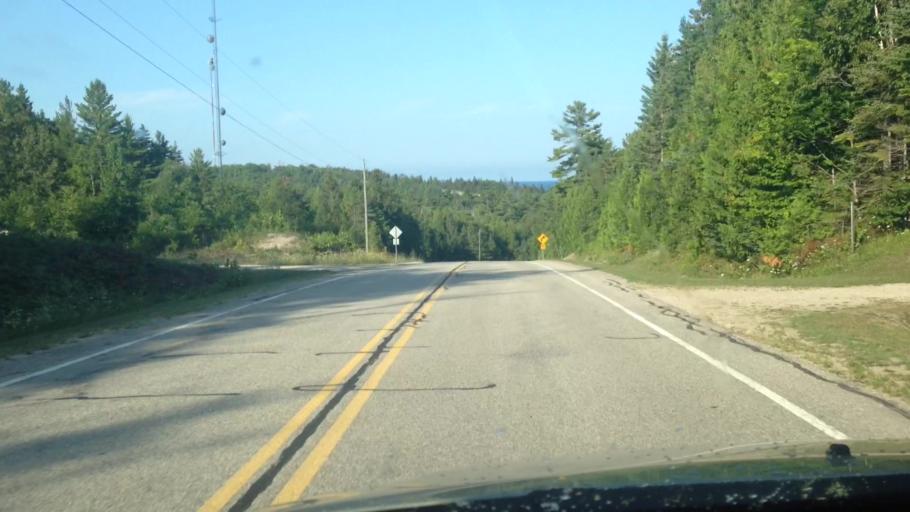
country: US
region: Michigan
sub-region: Mackinac County
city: Saint Ignace
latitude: 45.8934
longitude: -84.8244
